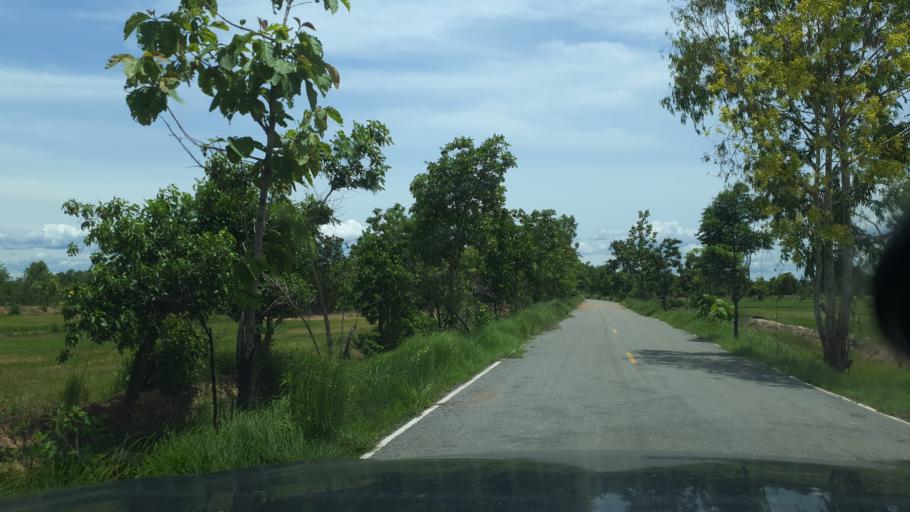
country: TH
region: Sukhothai
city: Ban Na
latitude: 17.1189
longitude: 99.6755
